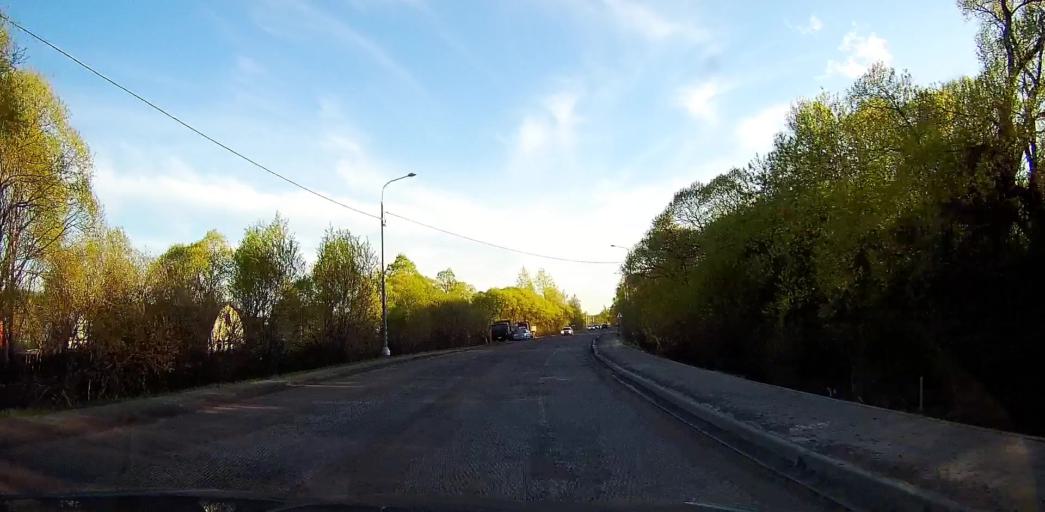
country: RU
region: Moskovskaya
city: Bronnitsy
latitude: 55.3065
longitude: 38.2129
